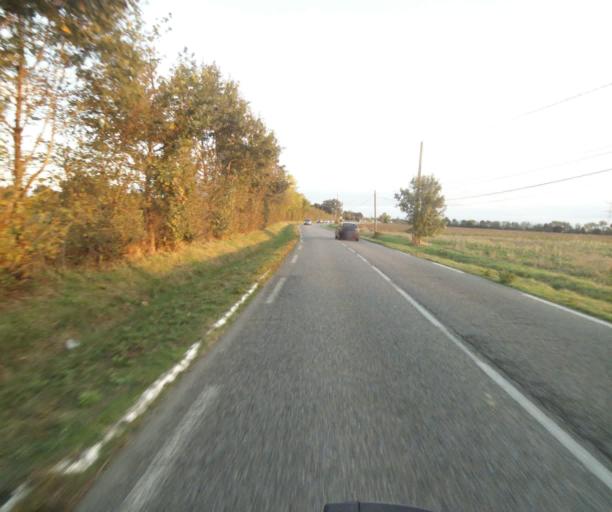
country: FR
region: Midi-Pyrenees
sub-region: Departement du Tarn-et-Garonne
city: Verdun-sur-Garonne
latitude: 43.8316
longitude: 1.2414
